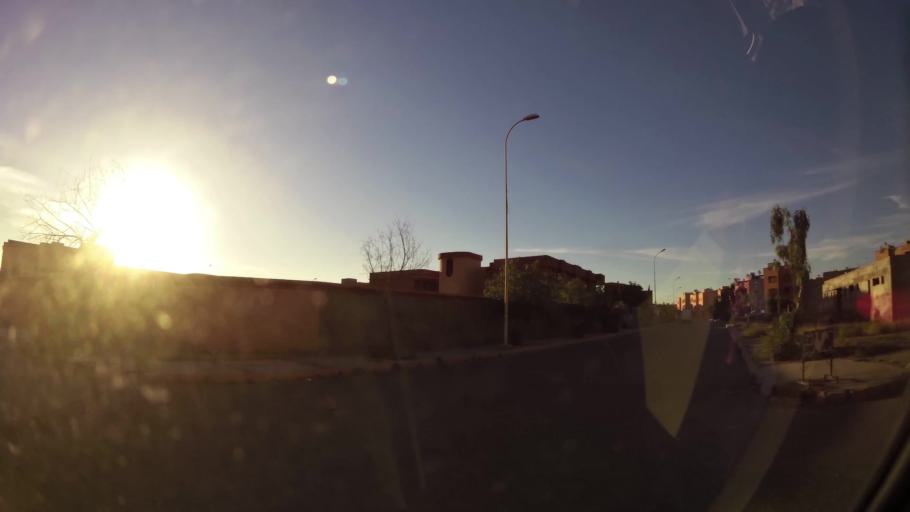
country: MA
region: Marrakech-Tensift-Al Haouz
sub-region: Marrakech
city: Marrakesh
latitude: 31.7443
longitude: -8.1099
